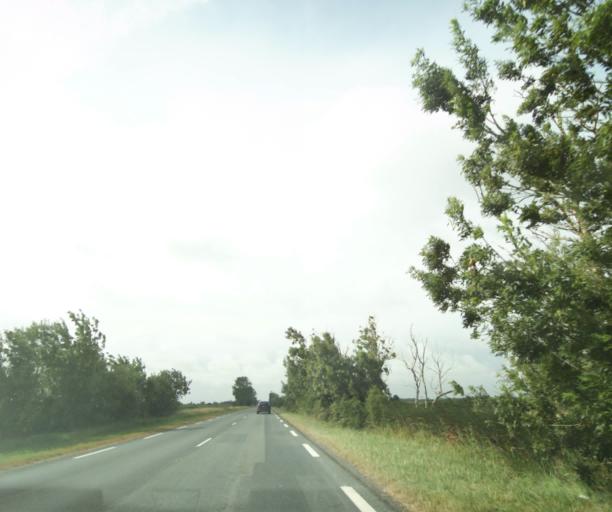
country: FR
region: Poitou-Charentes
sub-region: Departement de la Charente-Maritime
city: Andilly
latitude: 46.2588
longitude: -1.0667
